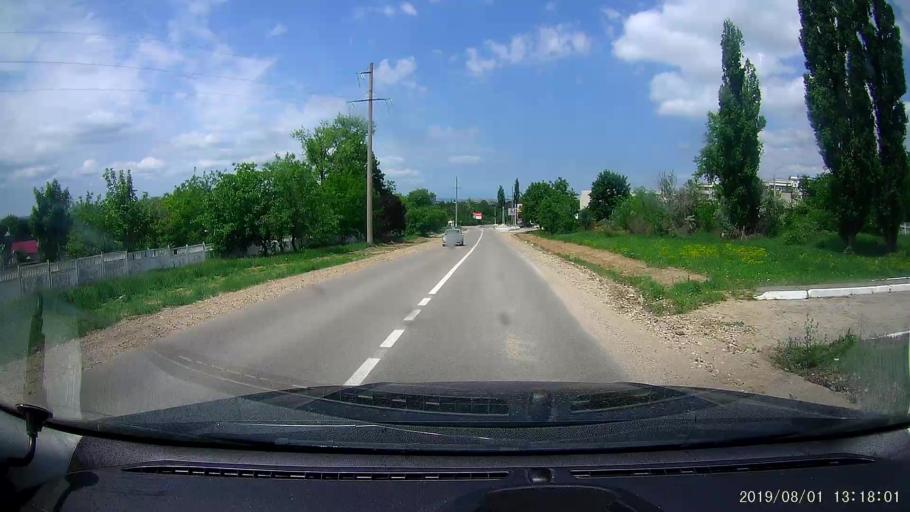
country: MD
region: Cahul
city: Cahul
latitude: 45.8937
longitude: 28.2057
